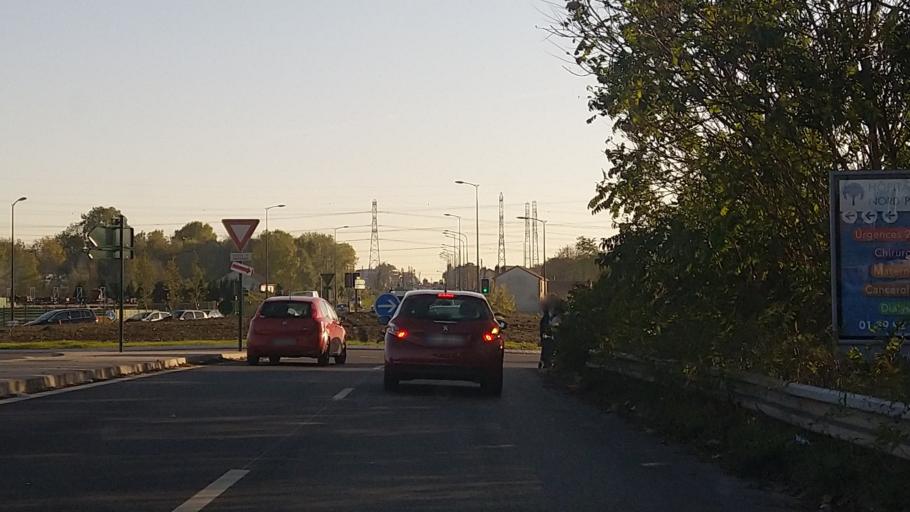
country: FR
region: Ile-de-France
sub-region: Departement du Val-d'Oise
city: Groslay
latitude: 48.9851
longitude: 2.3616
